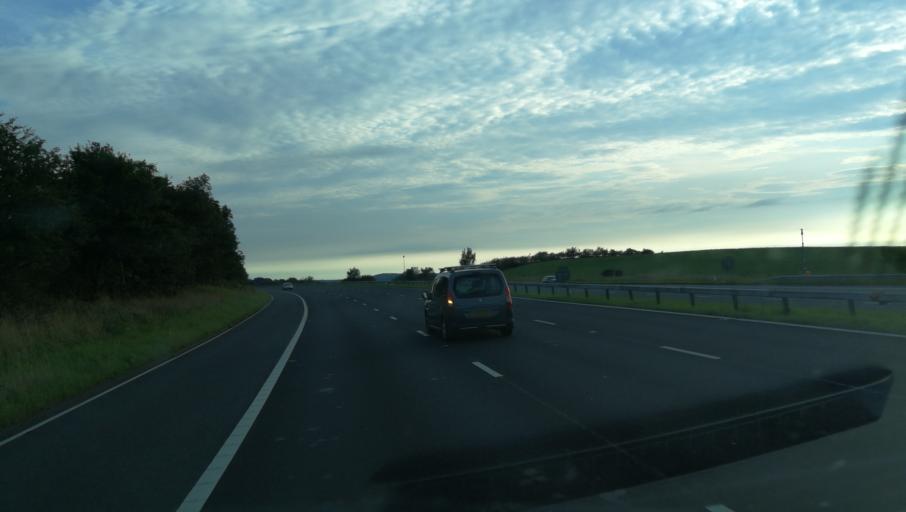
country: GB
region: England
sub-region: Cumbria
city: Kendal
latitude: 54.2691
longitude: -2.6809
